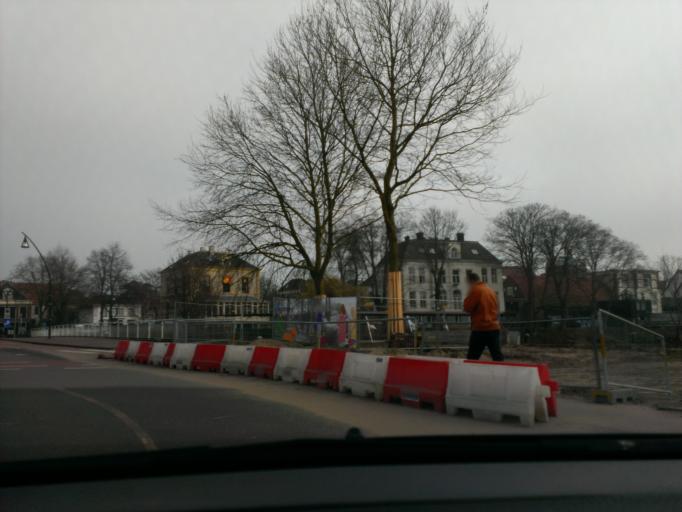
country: NL
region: Overijssel
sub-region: Gemeente Zwolle
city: Zwolle
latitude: 52.5122
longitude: 6.0867
